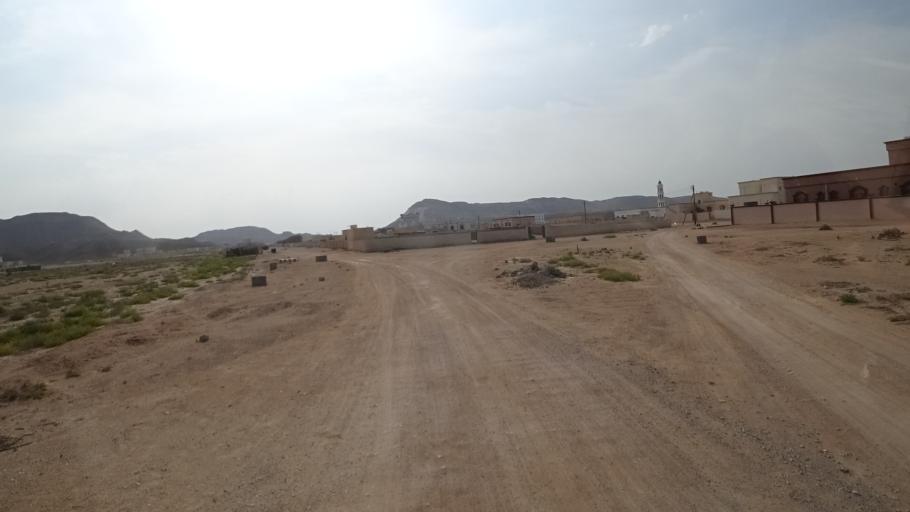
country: OM
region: Ash Sharqiyah
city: Sur
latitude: 22.4325
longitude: 59.8292
